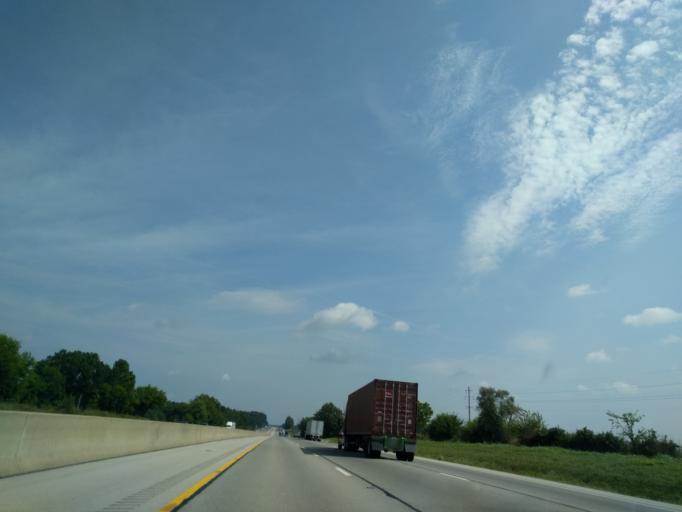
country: US
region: Kentucky
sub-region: Warren County
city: Plano
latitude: 36.8386
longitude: -86.4640
